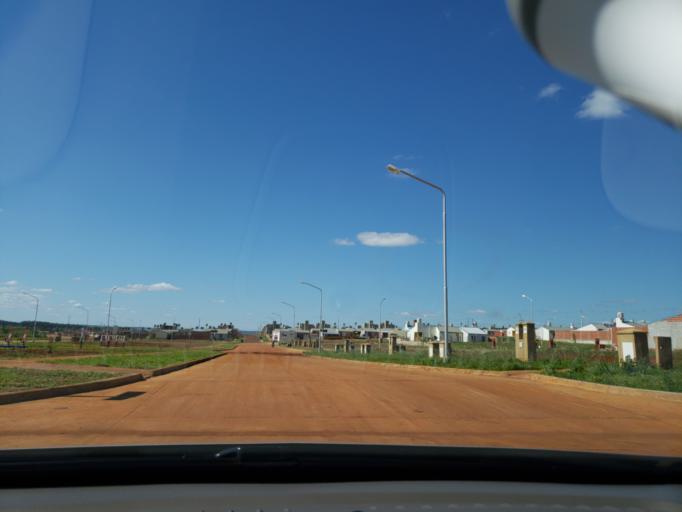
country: AR
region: Misiones
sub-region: Departamento de Capital
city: Posadas
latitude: -27.4061
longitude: -55.9873
